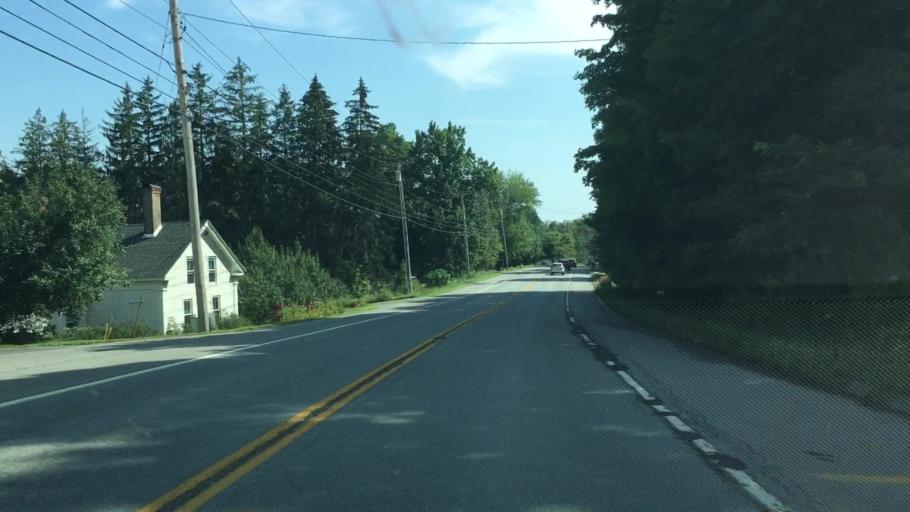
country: US
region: Maine
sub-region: Penobscot County
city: Orrington
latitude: 44.7199
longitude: -68.8451
